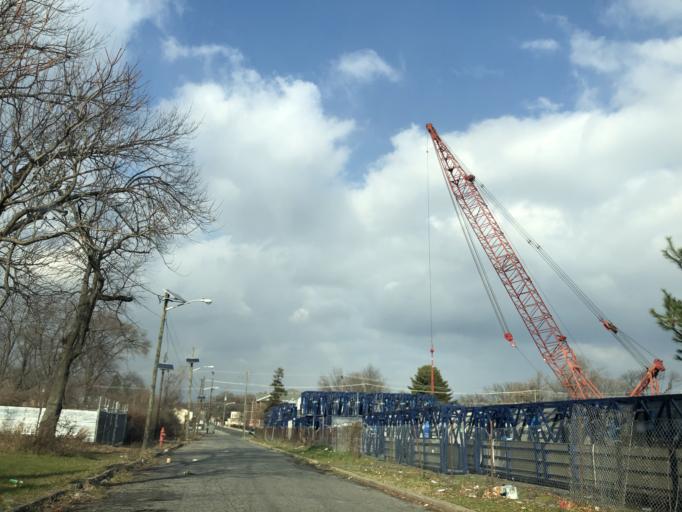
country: US
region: New Jersey
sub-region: Camden County
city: Wood-Lynne
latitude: 39.9182
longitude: -75.1078
